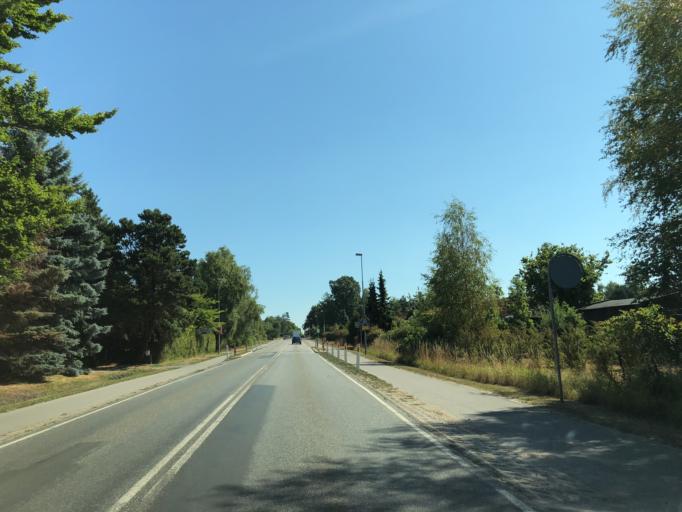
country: DK
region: Zealand
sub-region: Odsherred Kommune
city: Nykobing Sjaelland
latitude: 55.9423
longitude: 11.7379
